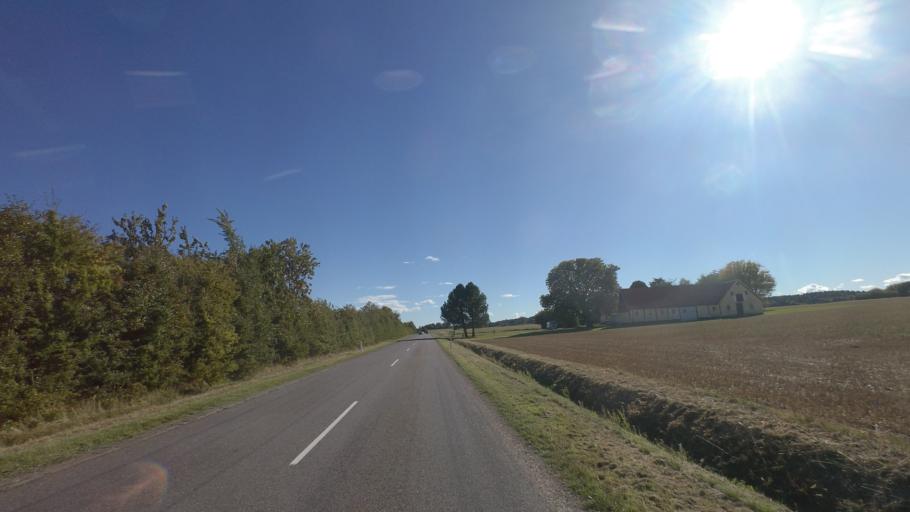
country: DK
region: Capital Region
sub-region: Bornholm Kommune
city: Nexo
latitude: 55.1122
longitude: 15.1099
